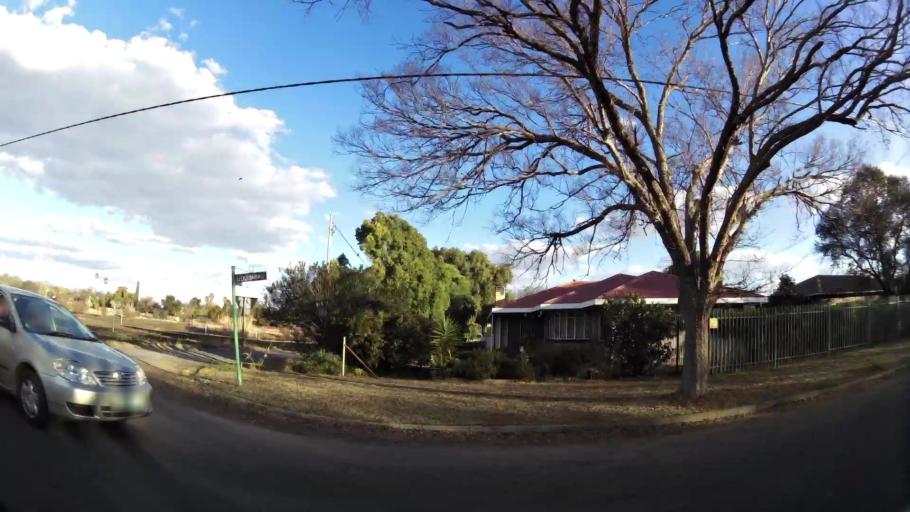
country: ZA
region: North-West
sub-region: Dr Kenneth Kaunda District Municipality
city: Potchefstroom
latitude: -26.7022
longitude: 27.0877
